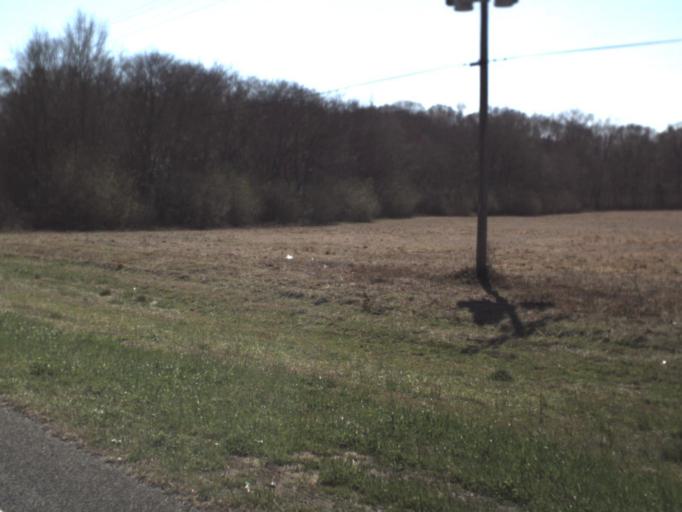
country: US
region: Florida
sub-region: Jackson County
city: Graceville
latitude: 30.9067
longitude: -85.3766
